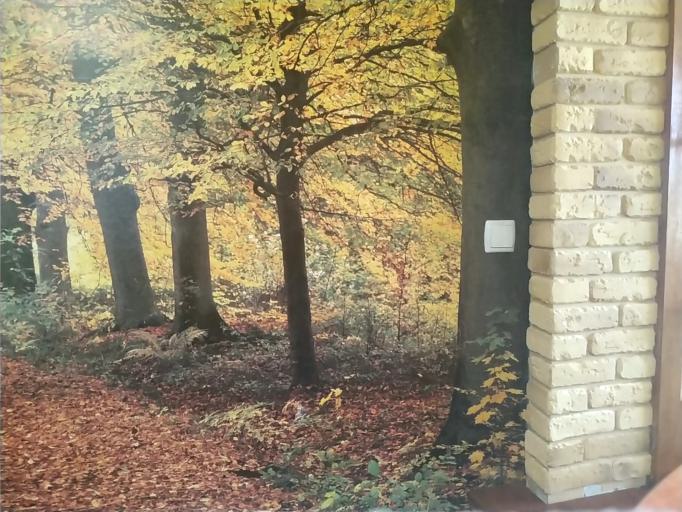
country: RU
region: Tverskaya
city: Vyshniy Volochek
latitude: 57.6746
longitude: 34.5245
